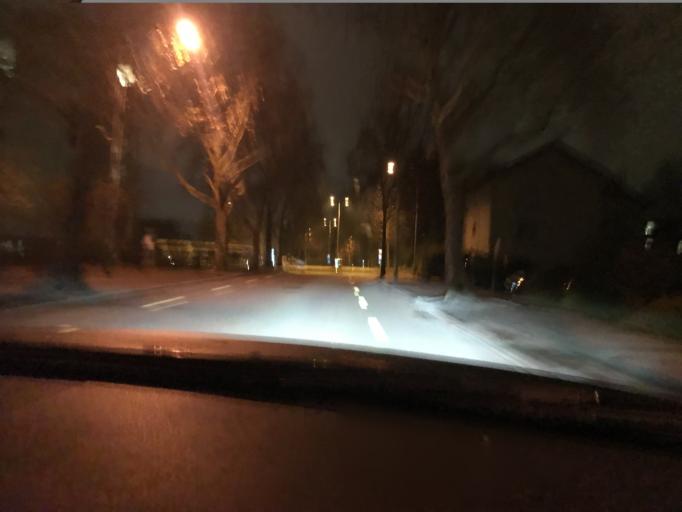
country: CH
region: Zurich
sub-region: Bezirk Buelach
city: Glattbrugg / Wydacker/Bettacker/Laettenwiesen
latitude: 47.4296
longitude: 8.5647
